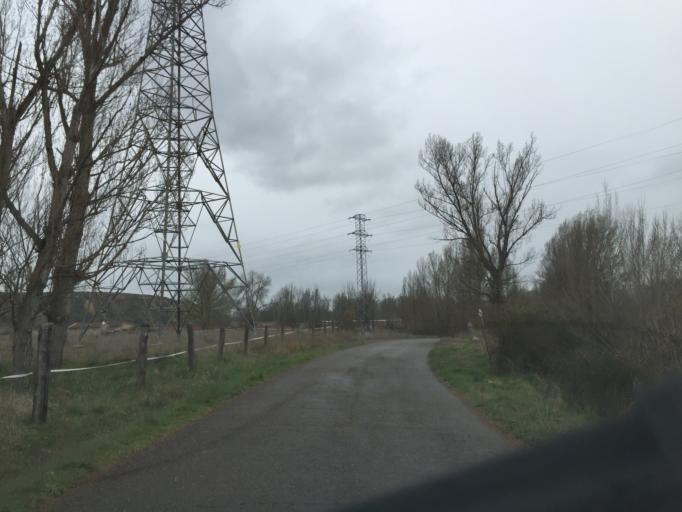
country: ES
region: Castille and Leon
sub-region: Provincia de Leon
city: Leon
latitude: 42.6021
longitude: -5.5455
